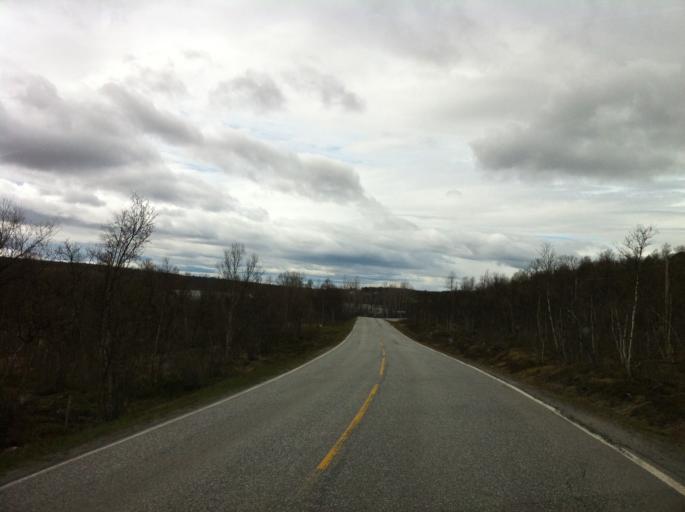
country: NO
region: Sor-Trondelag
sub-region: Roros
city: Roros
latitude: 62.5998
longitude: 11.4885
